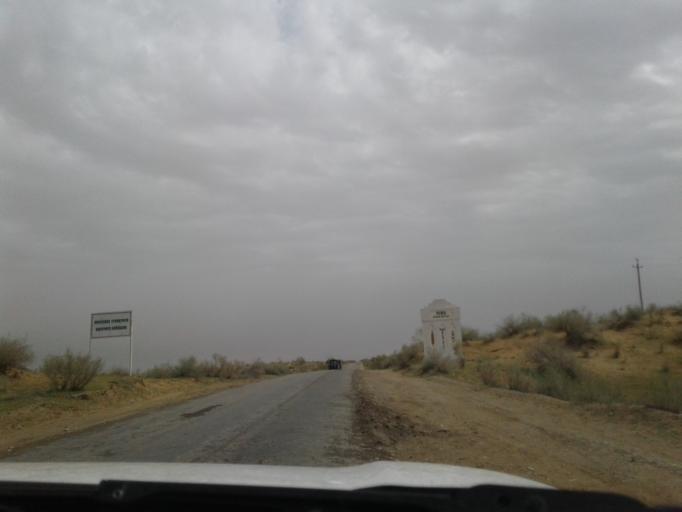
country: TM
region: Lebap
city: Atamyrat
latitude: 38.1595
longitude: 64.9391
